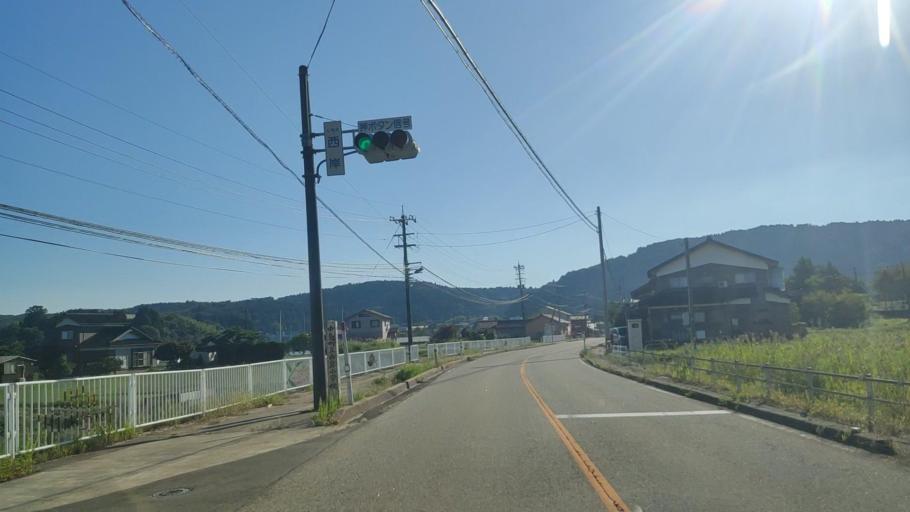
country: JP
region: Ishikawa
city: Nanao
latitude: 37.1484
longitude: 136.8760
